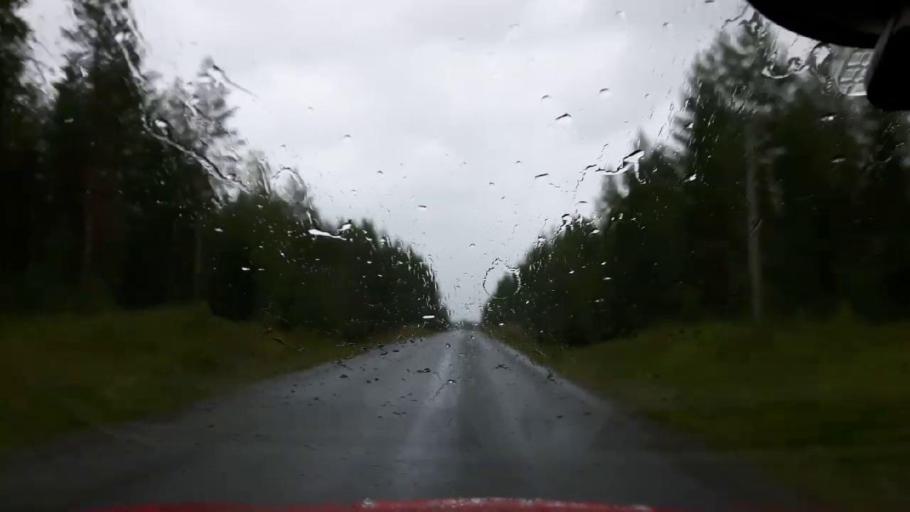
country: SE
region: Jaemtland
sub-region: OEstersunds Kommun
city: Brunflo
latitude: 62.9990
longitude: 14.7588
